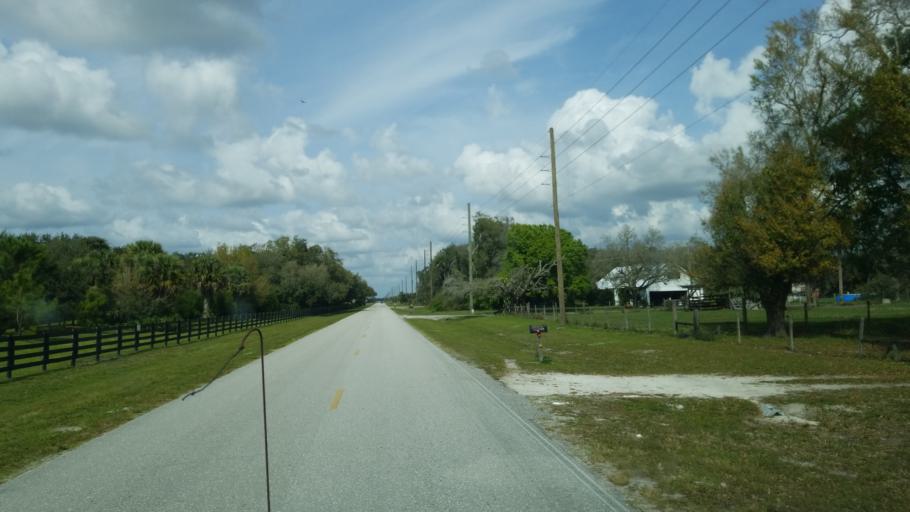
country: US
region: Florida
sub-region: Okeechobee County
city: Cypress Quarters
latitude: 27.4517
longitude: -80.7714
